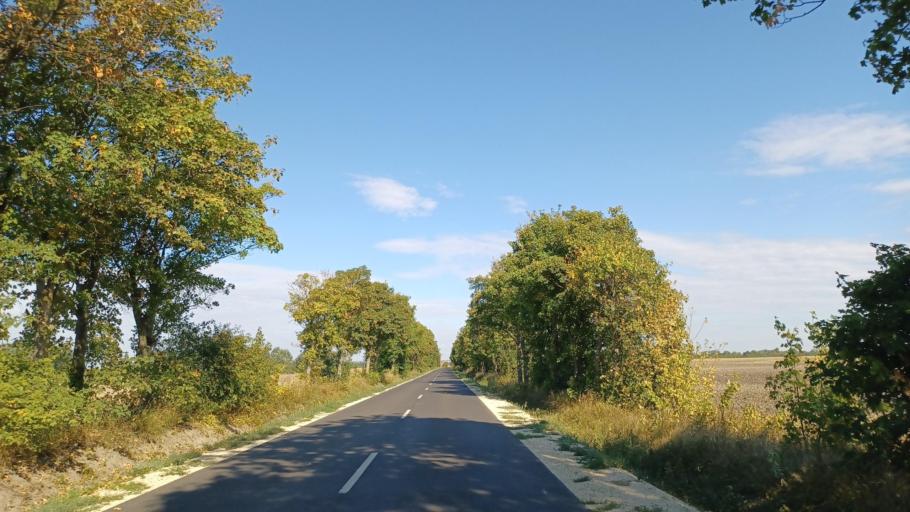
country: HU
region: Tolna
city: Dunaszentgyorgy
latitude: 46.5001
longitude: 18.8272
